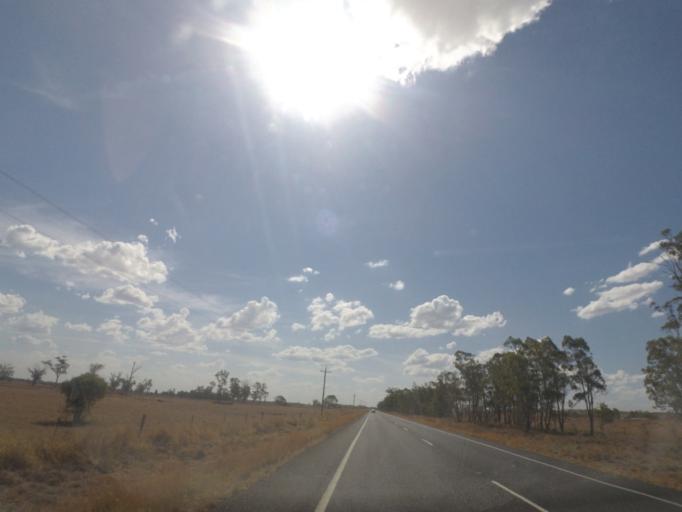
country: AU
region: Queensland
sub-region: Southern Downs
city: Stanthorpe
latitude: -28.4068
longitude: 151.2012
